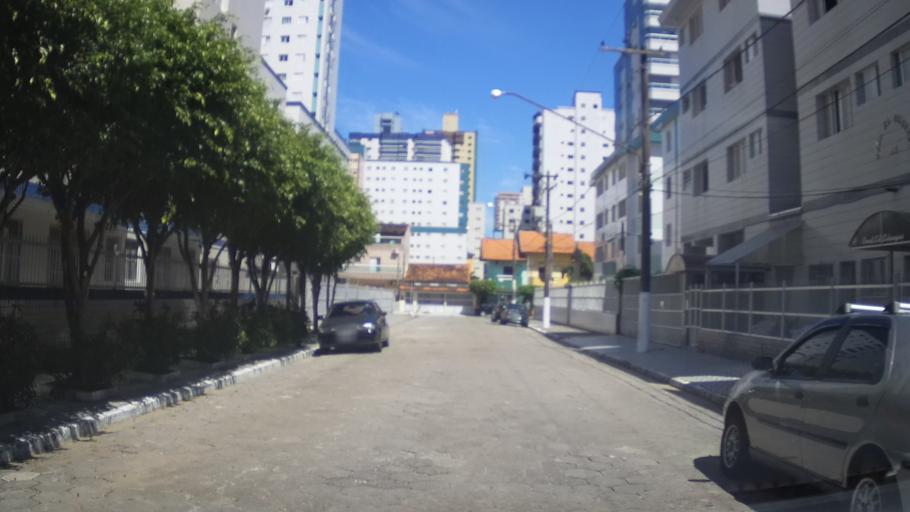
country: BR
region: Sao Paulo
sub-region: Praia Grande
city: Praia Grande
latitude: -24.0146
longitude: -46.4310
